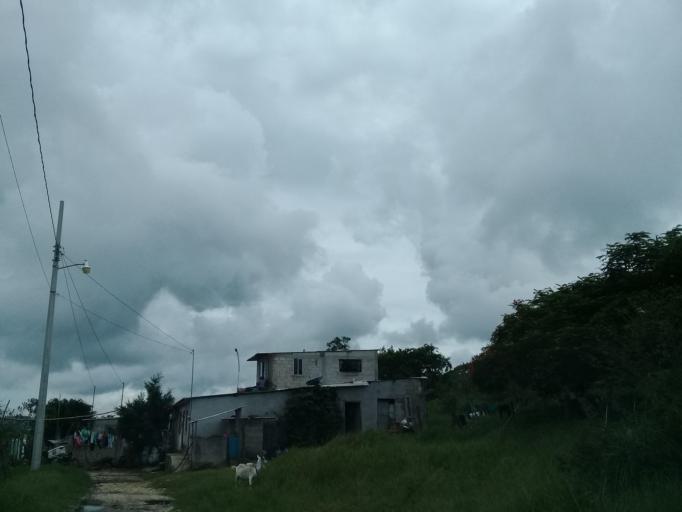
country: MX
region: Veracruz
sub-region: Emiliano Zapata
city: Dos Rios
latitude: 19.4643
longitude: -96.7864
